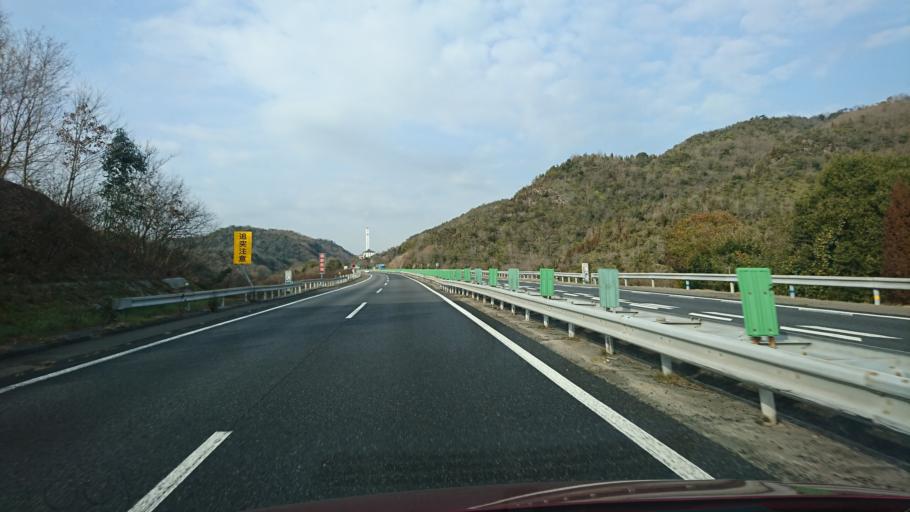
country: JP
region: Hyogo
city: Kariya
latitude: 34.7789
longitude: 134.2443
